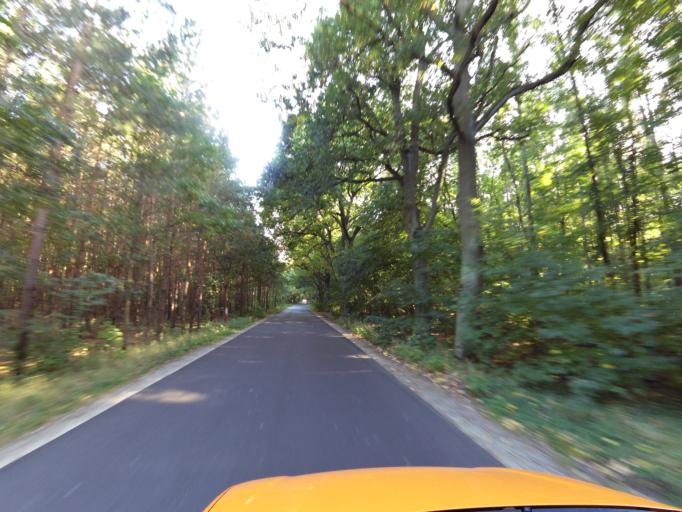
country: DE
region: Brandenburg
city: Potsdam
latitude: 52.4339
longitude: 13.0824
